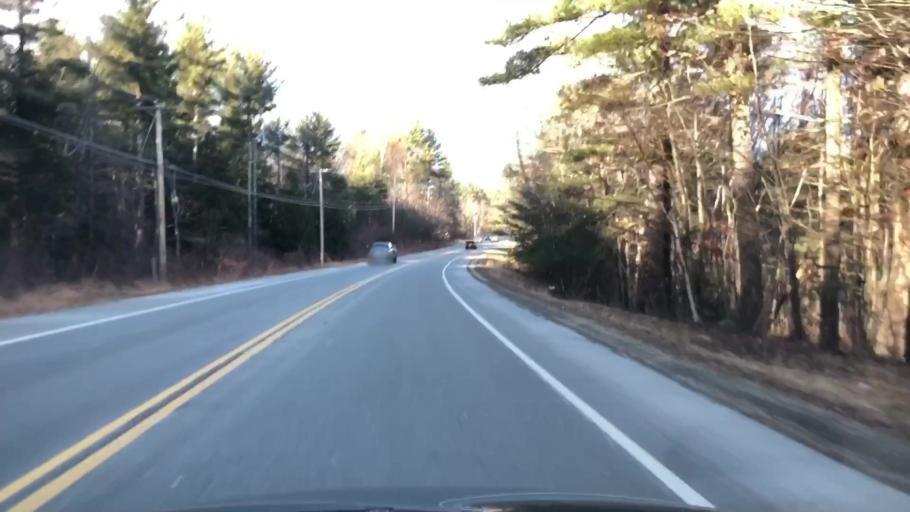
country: US
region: New Hampshire
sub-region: Hillsborough County
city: Milford
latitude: 42.7884
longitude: -71.6586
